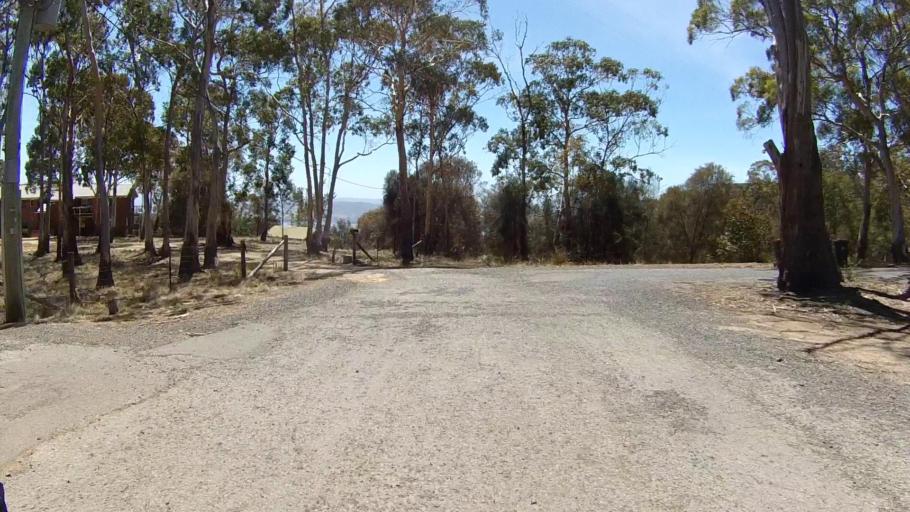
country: AU
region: Tasmania
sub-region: Clarence
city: Cambridge
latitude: -42.8459
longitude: 147.4319
